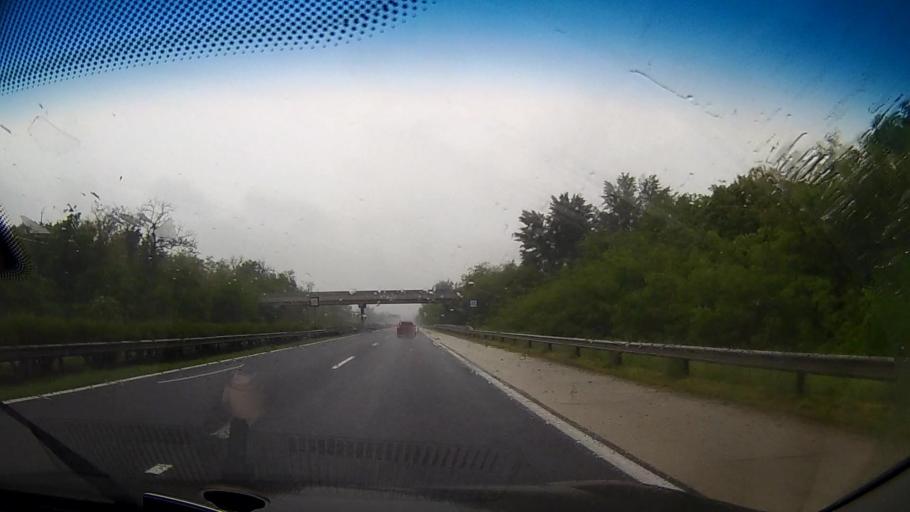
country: HU
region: Komarom-Esztergom
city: Vertesszolos
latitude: 47.6109
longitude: 18.3588
